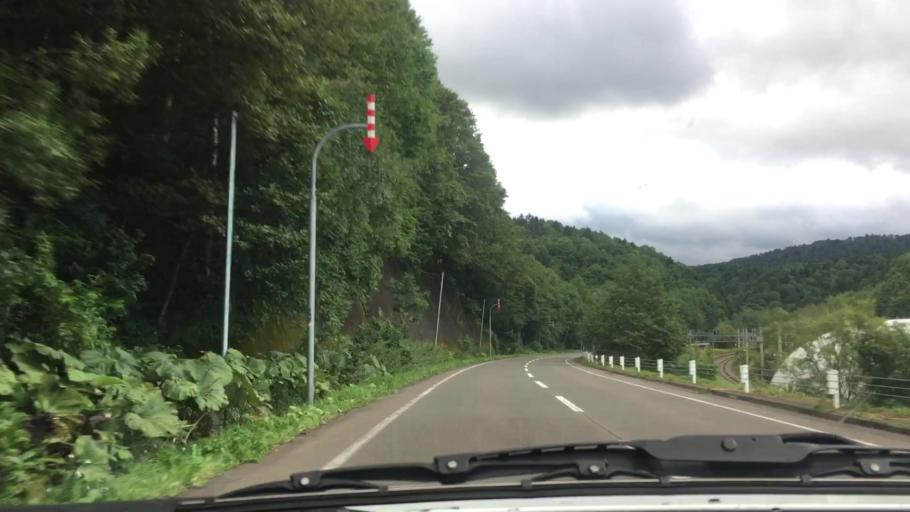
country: JP
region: Hokkaido
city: Shimo-furano
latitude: 43.0758
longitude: 142.6748
